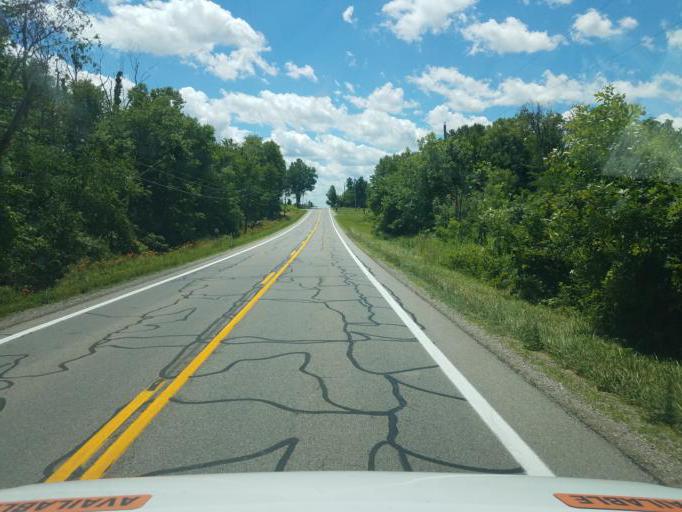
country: US
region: Ohio
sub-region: Morrow County
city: Mount Gilead
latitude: 40.6097
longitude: -82.8232
